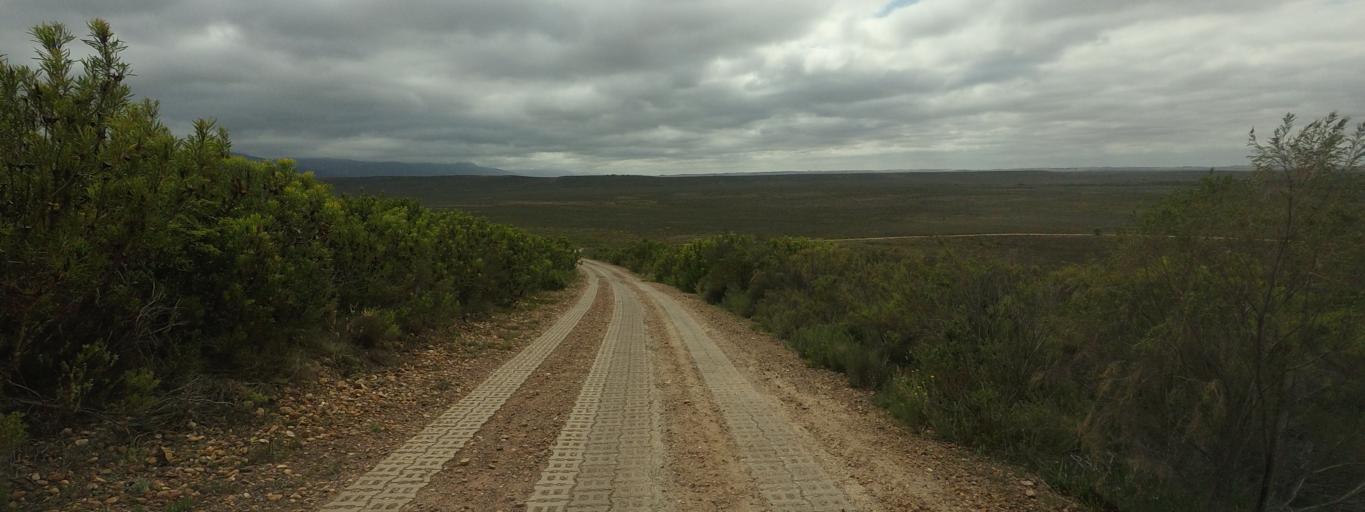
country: ZA
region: Western Cape
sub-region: Overberg District Municipality
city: Swellendam
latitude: -34.0626
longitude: 20.4354
